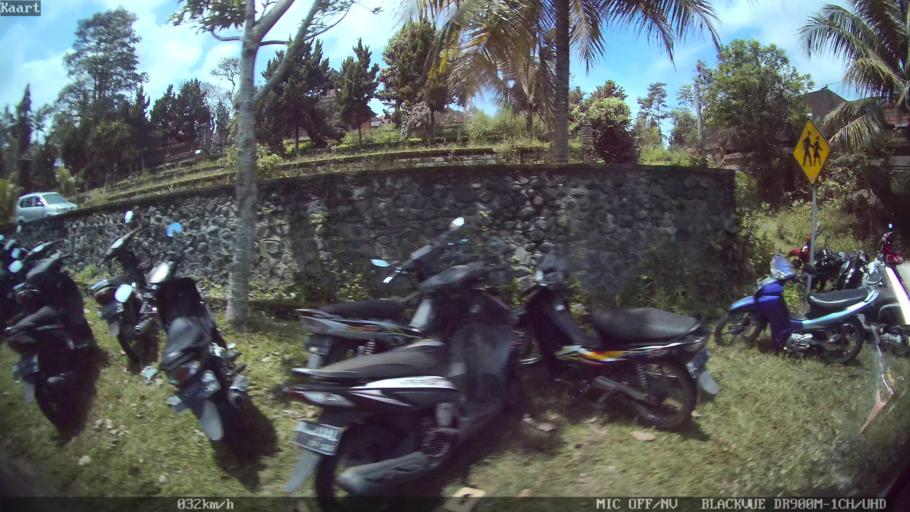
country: ID
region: Bali
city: Banjar Kelodan
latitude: -8.4973
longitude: 115.3679
